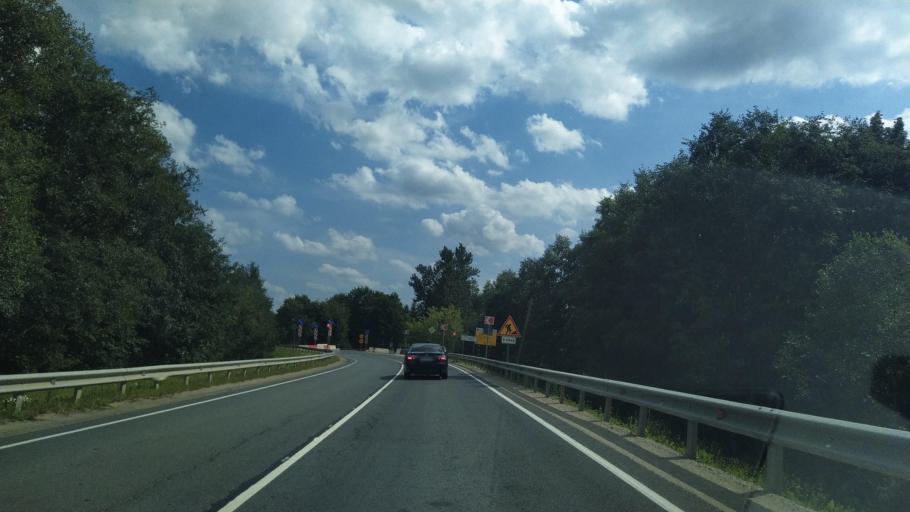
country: RU
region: Pskov
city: Pskov
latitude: 57.7142
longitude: 28.8498
